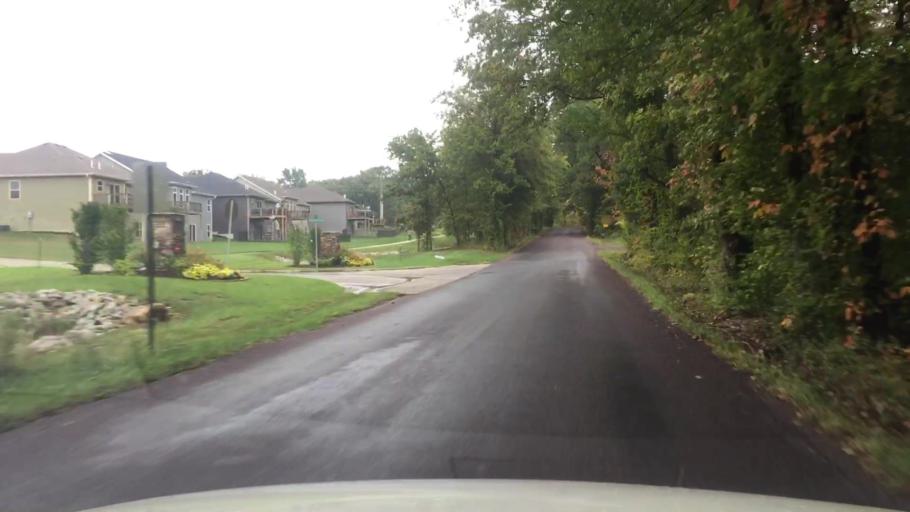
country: US
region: Missouri
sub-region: Boone County
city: Columbia
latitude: 38.8701
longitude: -92.3738
